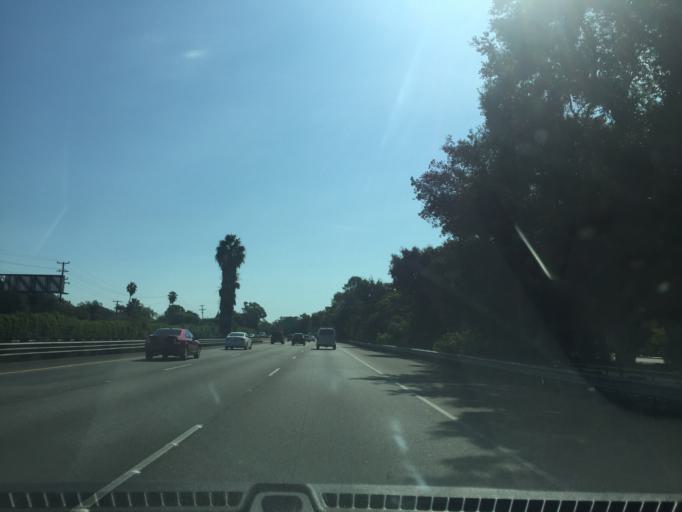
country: US
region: California
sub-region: Santa Barbara County
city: Mission Canyon
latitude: 34.4320
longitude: -119.7458
